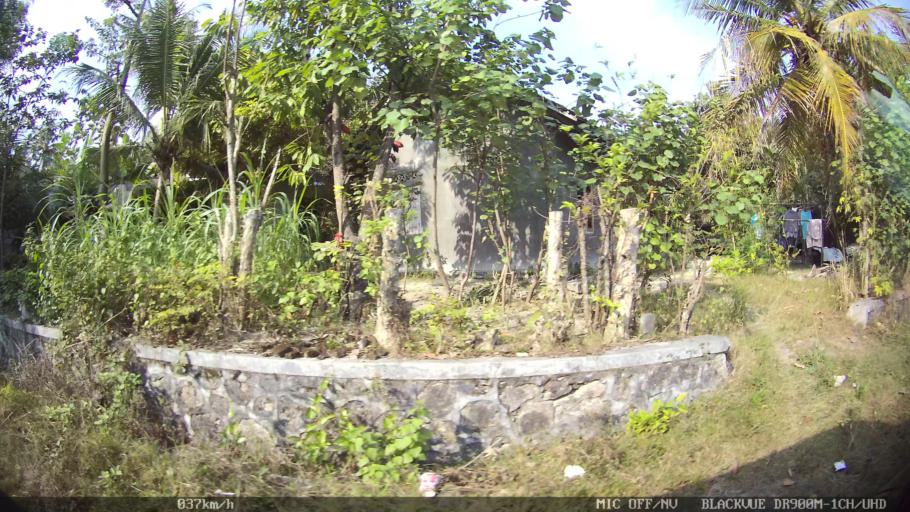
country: ID
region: Daerah Istimewa Yogyakarta
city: Bantul
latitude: -7.8645
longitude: 110.3188
